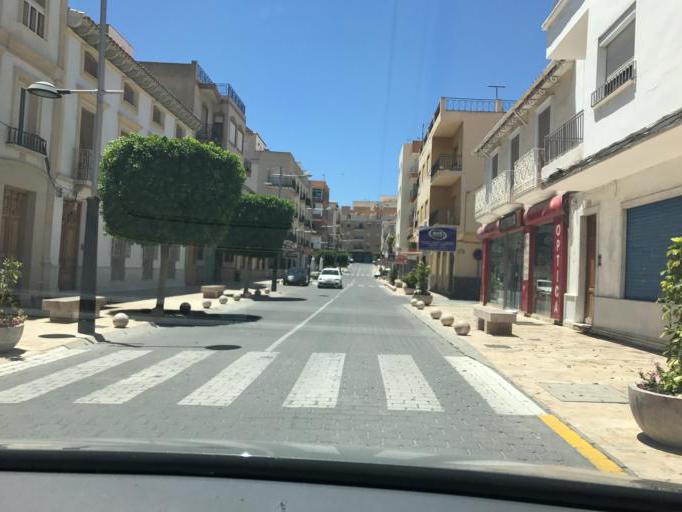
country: ES
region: Andalusia
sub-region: Provincia de Almeria
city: Albox
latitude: 37.3876
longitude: -2.1464
